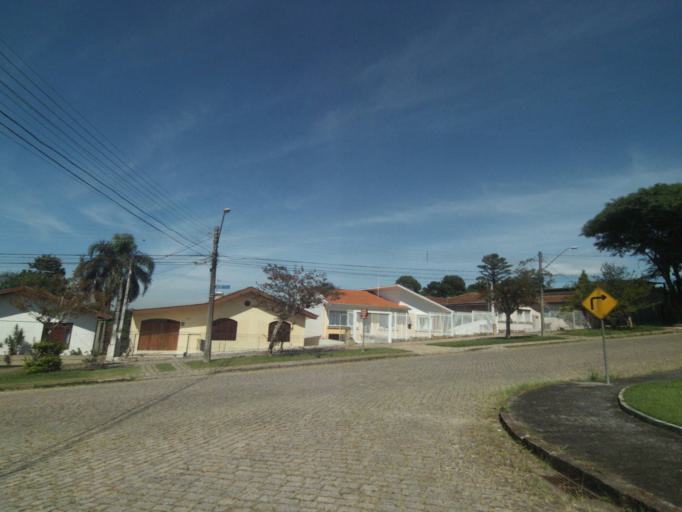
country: BR
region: Parana
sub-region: Curitiba
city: Curitiba
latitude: -25.4598
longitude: -49.2458
